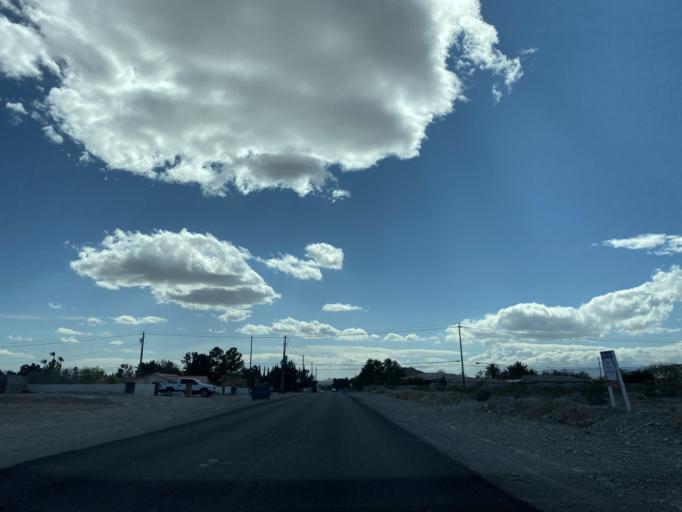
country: US
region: Nevada
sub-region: Clark County
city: Summerlin South
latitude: 36.2661
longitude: -115.2884
